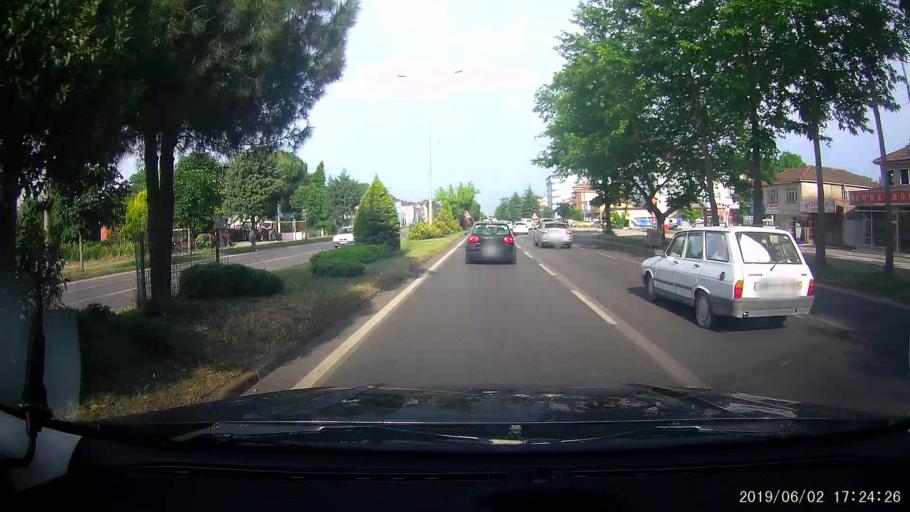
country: TR
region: Samsun
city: Carsamba
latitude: 41.2056
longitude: 36.7018
